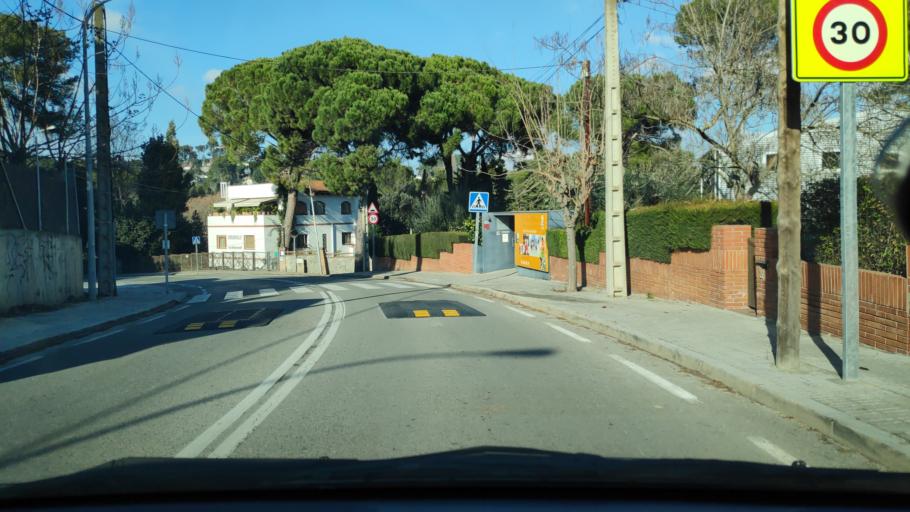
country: ES
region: Catalonia
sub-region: Provincia de Barcelona
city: Sant Cugat del Valles
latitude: 41.4988
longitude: 2.0884
